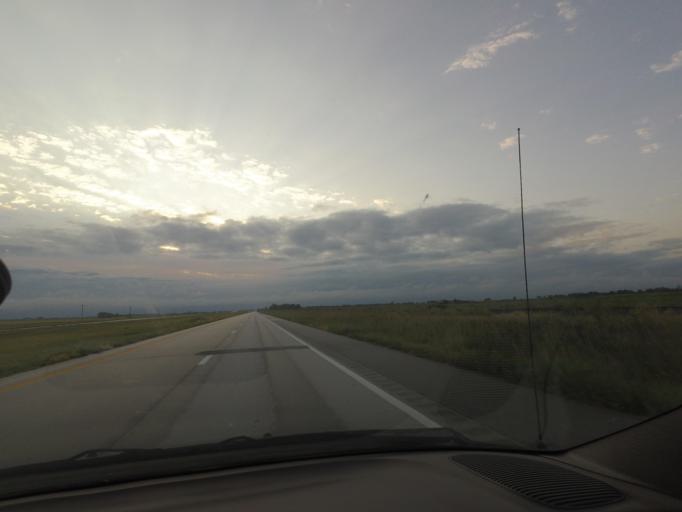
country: US
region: Missouri
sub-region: Shelby County
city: Shelbina
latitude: 39.7074
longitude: -92.0985
